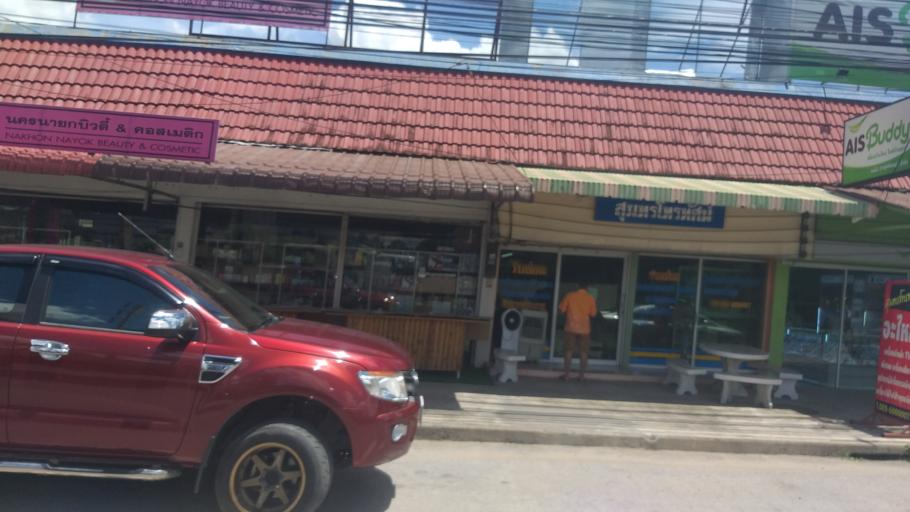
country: TH
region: Nakhon Nayok
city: Ban Na
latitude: 14.2624
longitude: 101.0673
